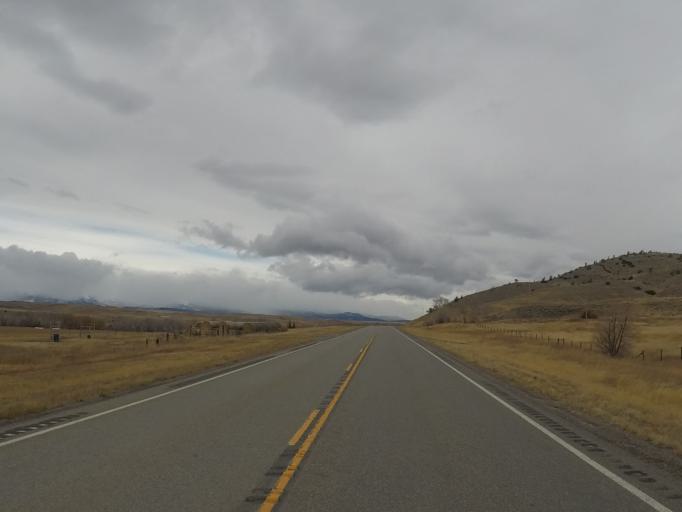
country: US
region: Montana
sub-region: Sweet Grass County
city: Big Timber
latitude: 45.8760
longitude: -109.9507
